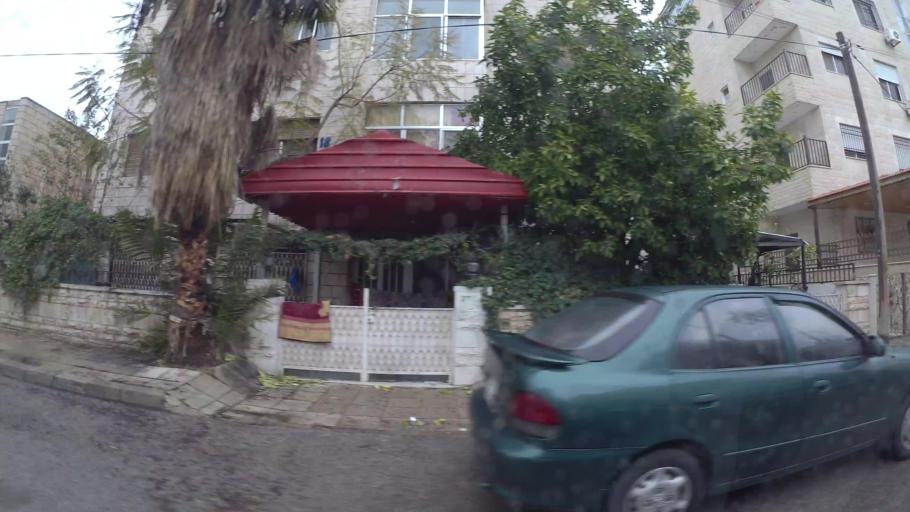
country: JO
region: Amman
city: Amman
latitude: 31.9728
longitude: 35.9156
